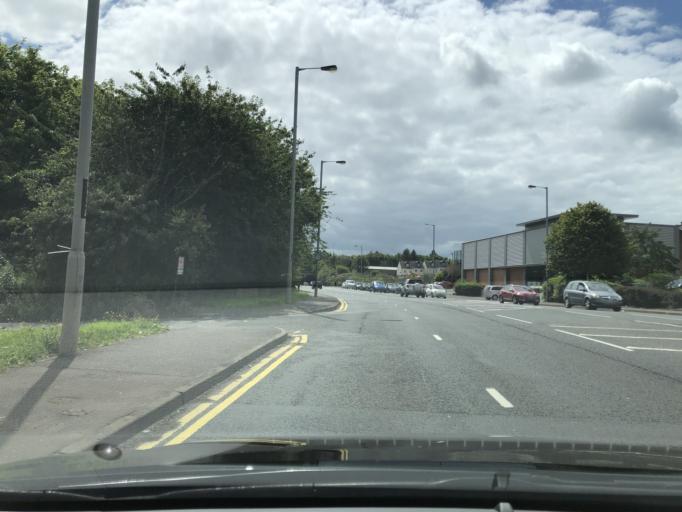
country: GB
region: Northern Ireland
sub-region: Newtownabbey District
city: Newtownabbey
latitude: 54.6515
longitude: -5.9177
